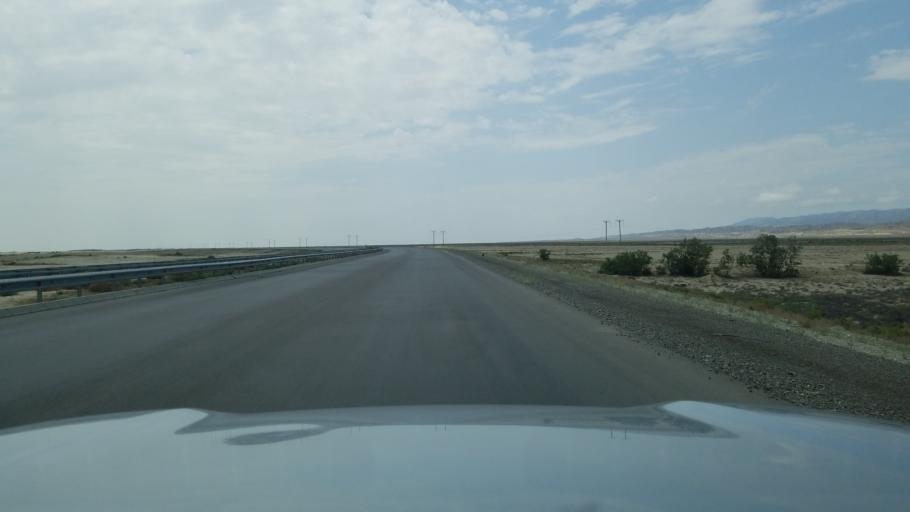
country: TM
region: Balkan
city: Gazanjyk
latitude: 39.2643
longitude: 55.1203
